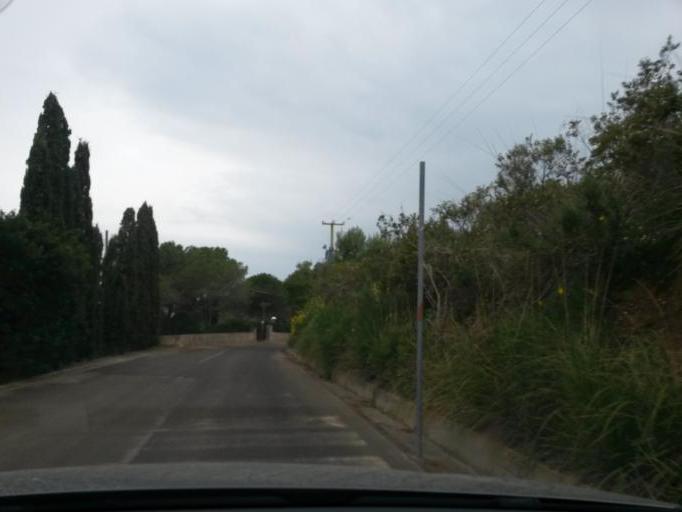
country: IT
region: Tuscany
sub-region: Provincia di Livorno
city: Capoliveri
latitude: 42.7502
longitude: 10.3634
